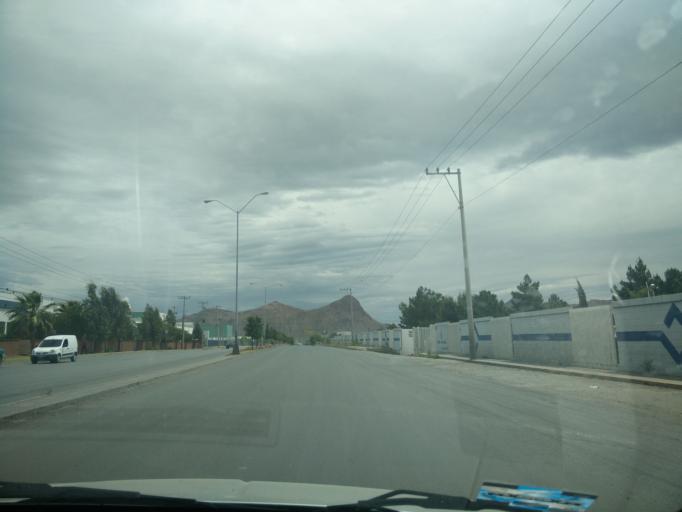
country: MX
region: Chihuahua
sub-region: Chihuahua
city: Chihuahua
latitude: 28.7096
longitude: -106.1126
